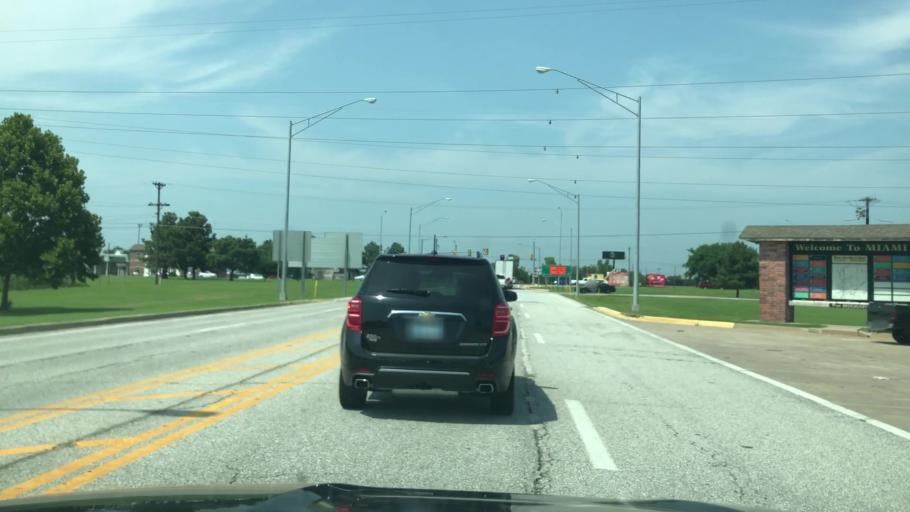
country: US
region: Oklahoma
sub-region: Ottawa County
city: Miami
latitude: 36.8694
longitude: -94.8518
